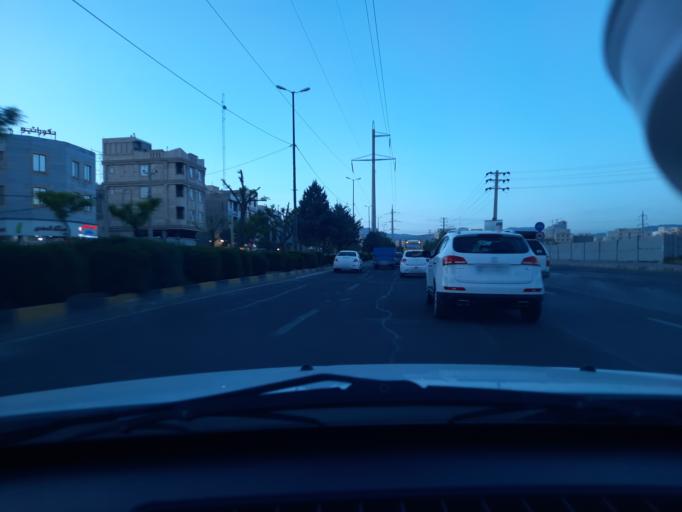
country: IR
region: Qazvin
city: Qazvin
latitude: 36.3022
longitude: 50.0105
